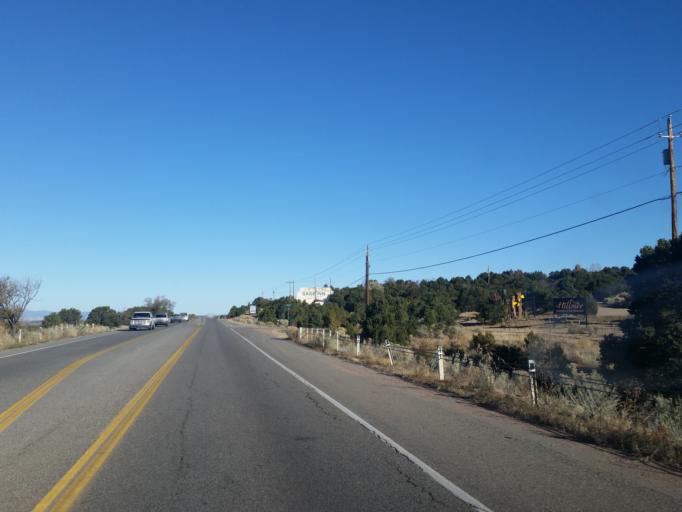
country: US
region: New Mexico
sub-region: Santa Fe County
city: Santa Fe
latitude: 35.6273
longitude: -105.9215
